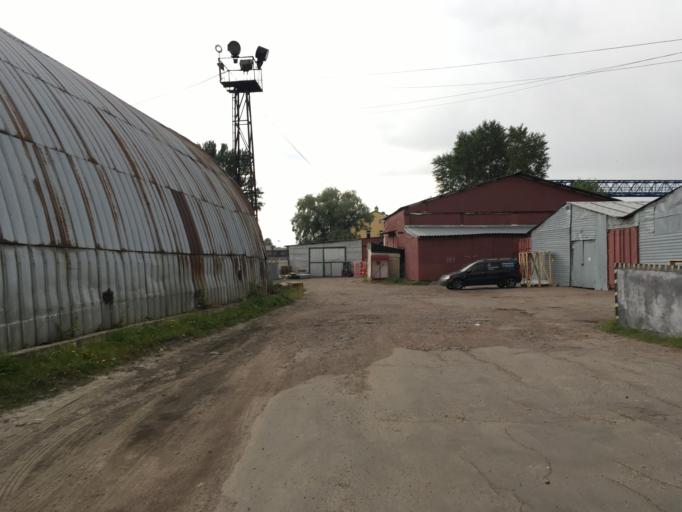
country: RU
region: St.-Petersburg
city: Centralniy
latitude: 59.9029
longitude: 30.3520
